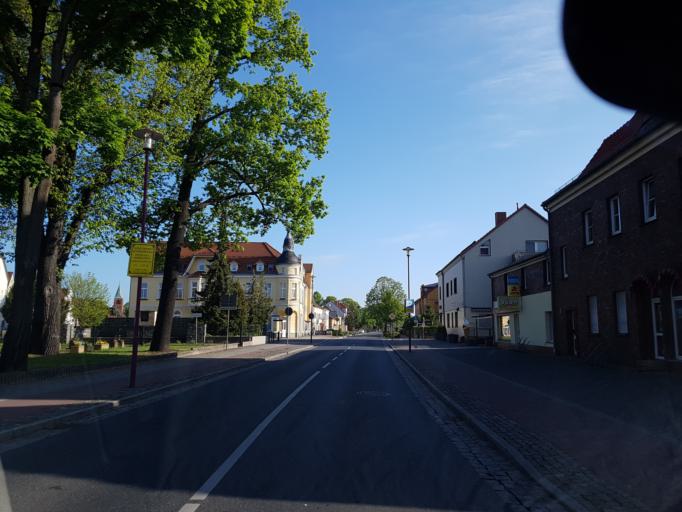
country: DE
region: Brandenburg
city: Grossraschen
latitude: 51.5881
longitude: 14.0110
